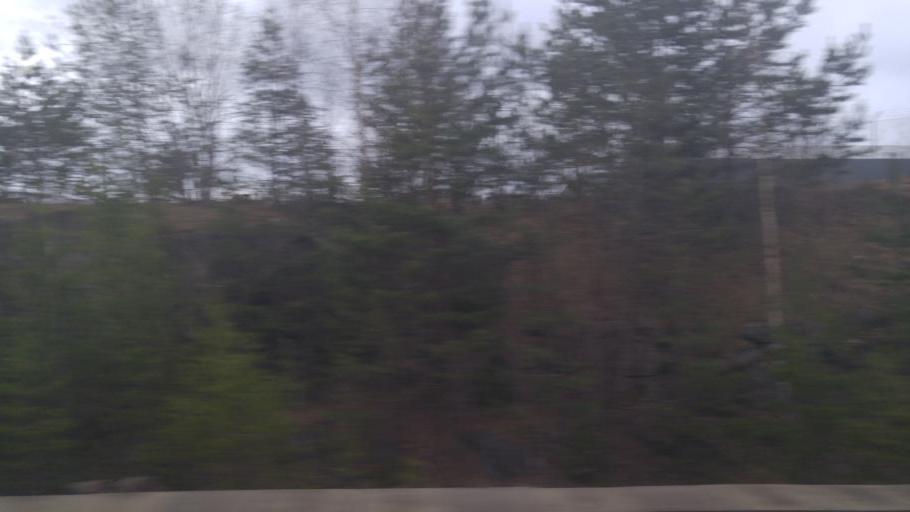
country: NO
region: Akershus
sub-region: Nannestad
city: Teigebyen
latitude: 60.2069
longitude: 11.1047
